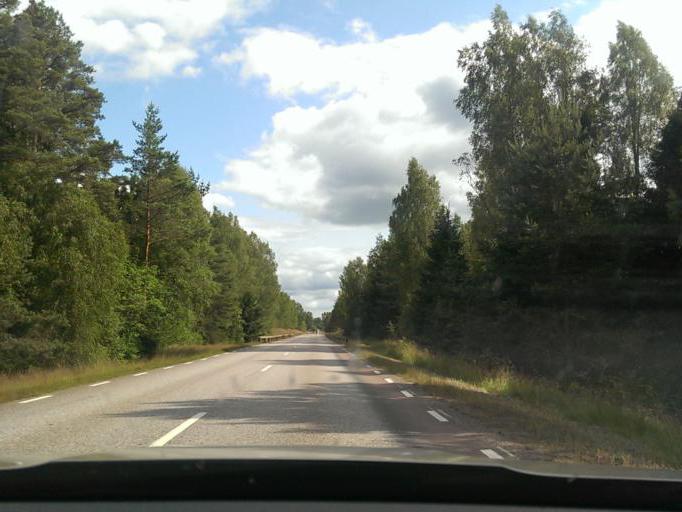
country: SE
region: Kronoberg
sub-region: Ljungby Kommun
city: Lagan
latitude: 56.9267
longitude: 13.9842
